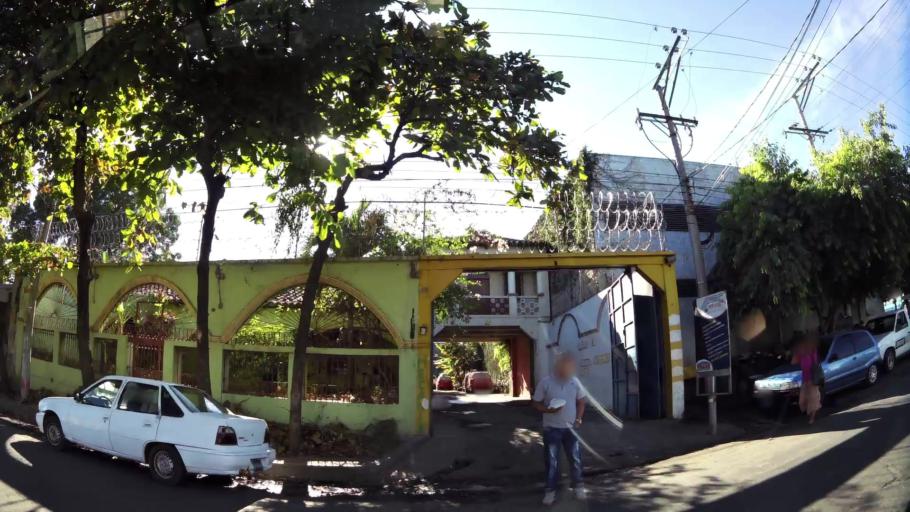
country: SV
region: Santa Ana
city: Santa Ana
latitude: 13.9855
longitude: -89.5691
